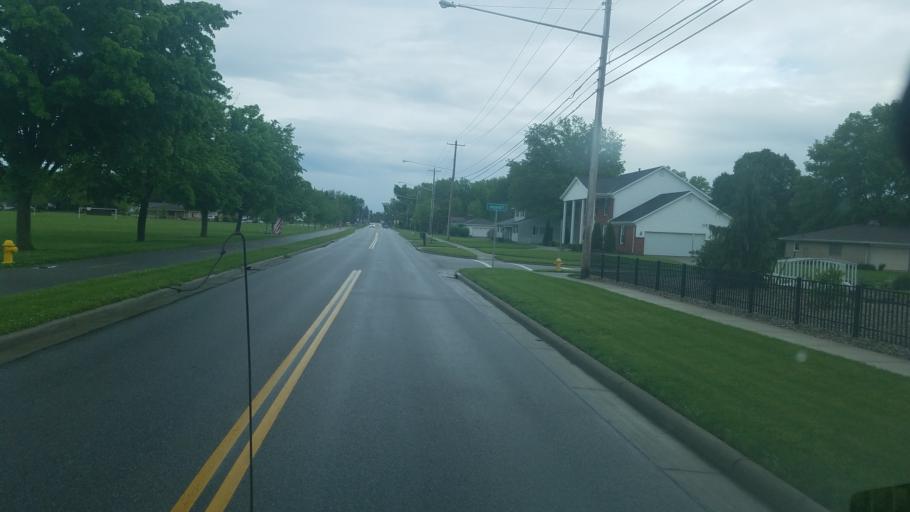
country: US
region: Ohio
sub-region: Wayne County
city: Wooster
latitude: 40.8331
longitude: -81.9390
